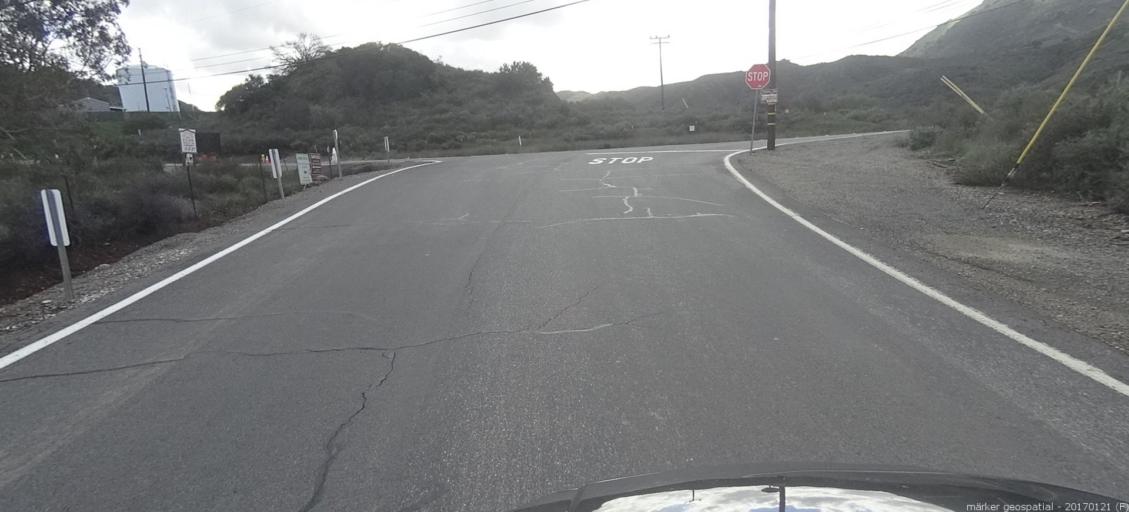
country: US
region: California
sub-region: Orange County
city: Foothill Ranch
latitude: 33.7498
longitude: -117.6720
